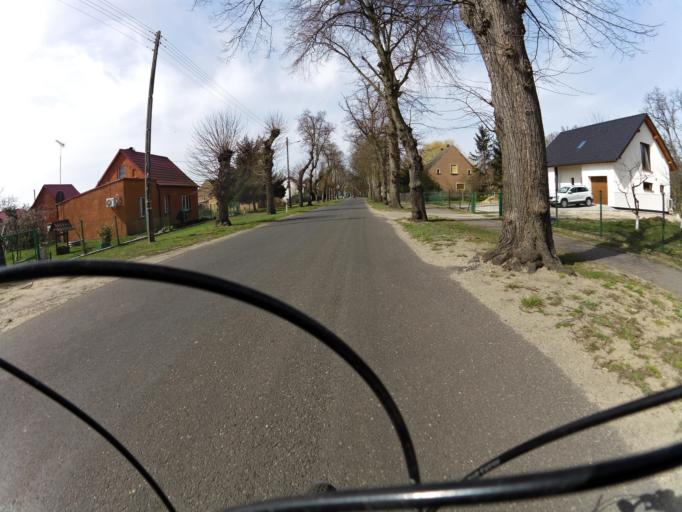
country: PL
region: West Pomeranian Voivodeship
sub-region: Powiat mysliborski
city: Boleszkowice
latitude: 52.6725
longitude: 14.5447
